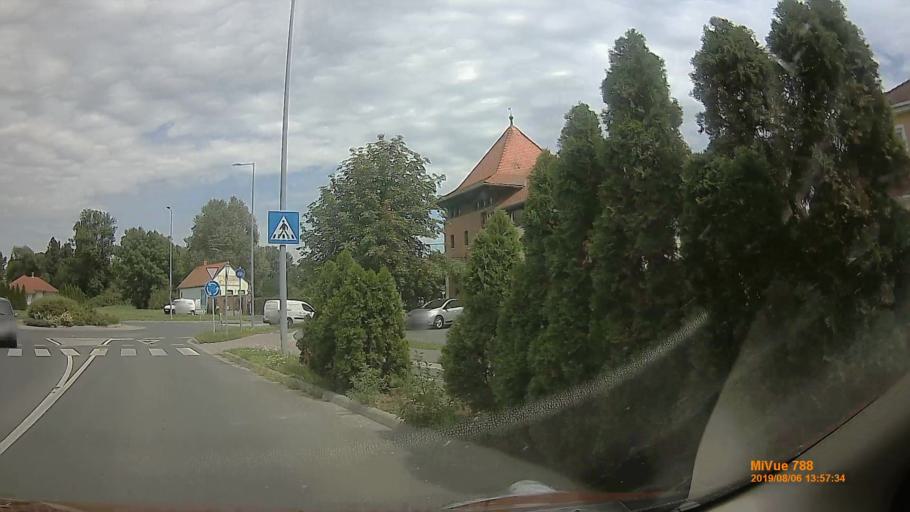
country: HU
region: Vas
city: Szombathely
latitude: 47.2502
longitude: 16.6071
